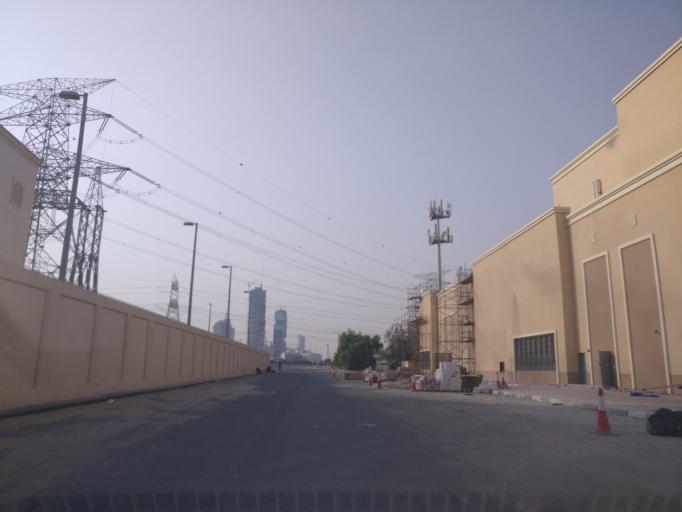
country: AE
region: Dubai
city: Dubai
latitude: 25.0658
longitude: 55.1932
